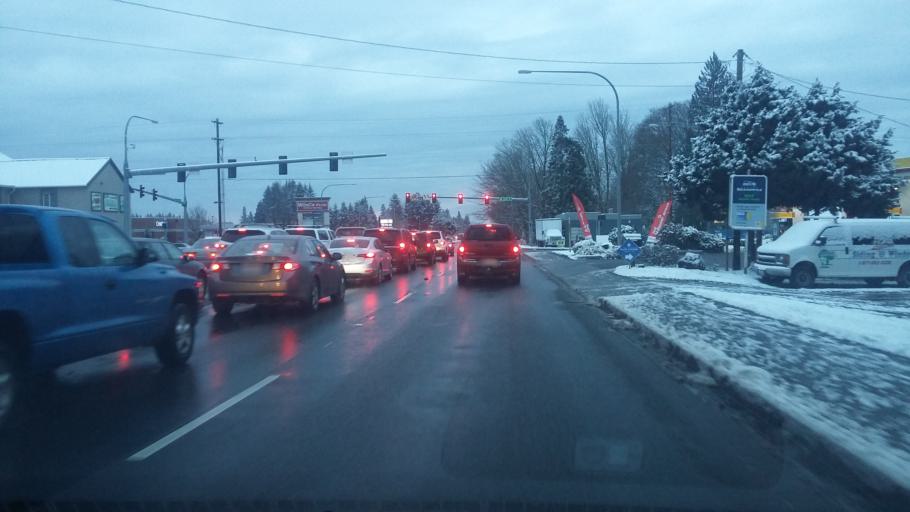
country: US
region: Washington
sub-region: Clark County
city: Brush Prairie
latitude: 45.7072
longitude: -122.5526
